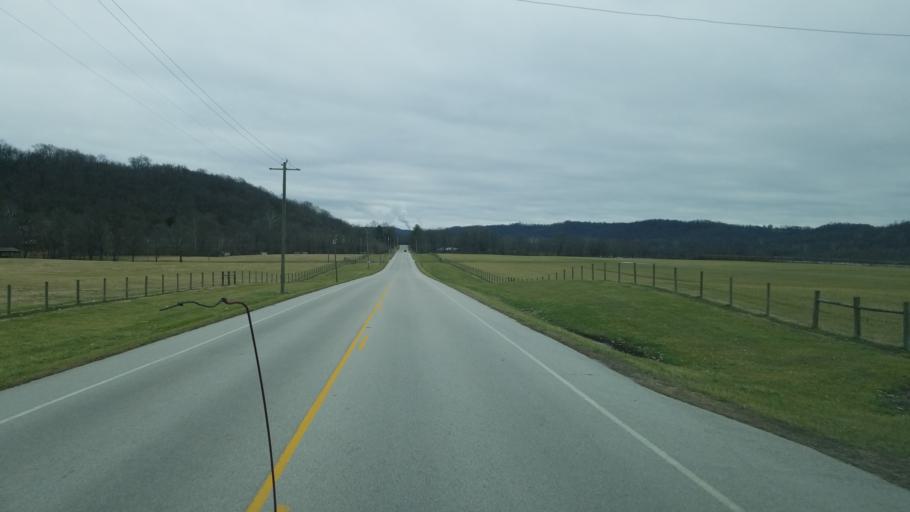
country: US
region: Ohio
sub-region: Brown County
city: Ripley
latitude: 38.7784
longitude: -83.9212
